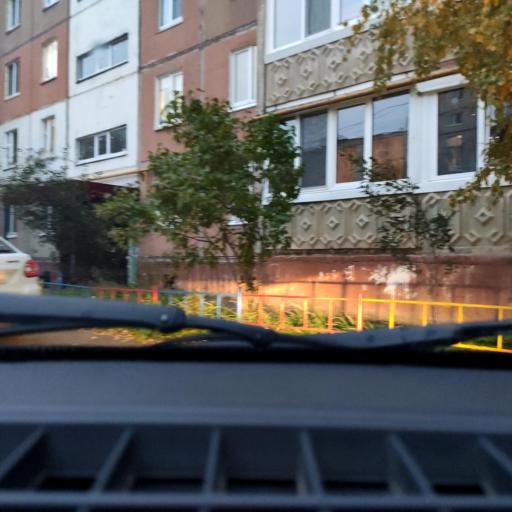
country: RU
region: Bashkortostan
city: Ufa
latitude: 54.7614
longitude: 56.0574
